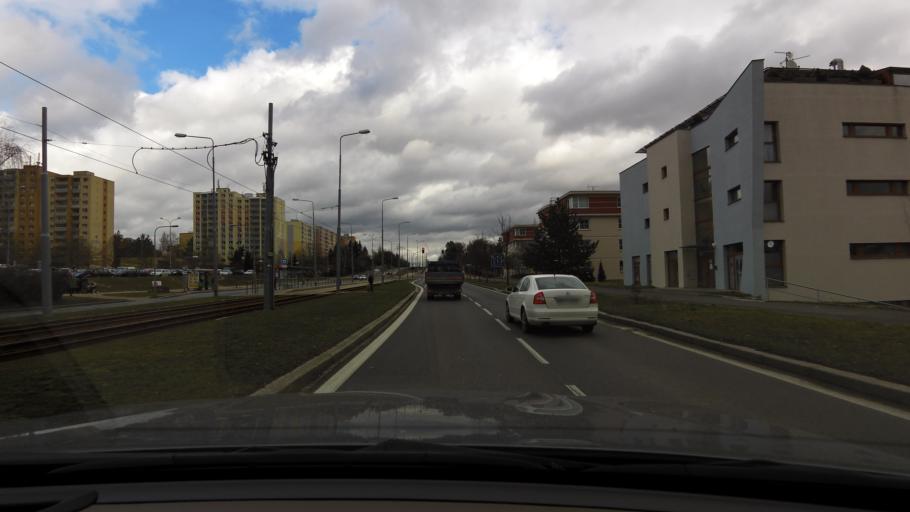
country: CZ
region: Plzensky
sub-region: Okres Plzen-Mesto
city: Pilsen
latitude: 49.7784
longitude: 13.3815
